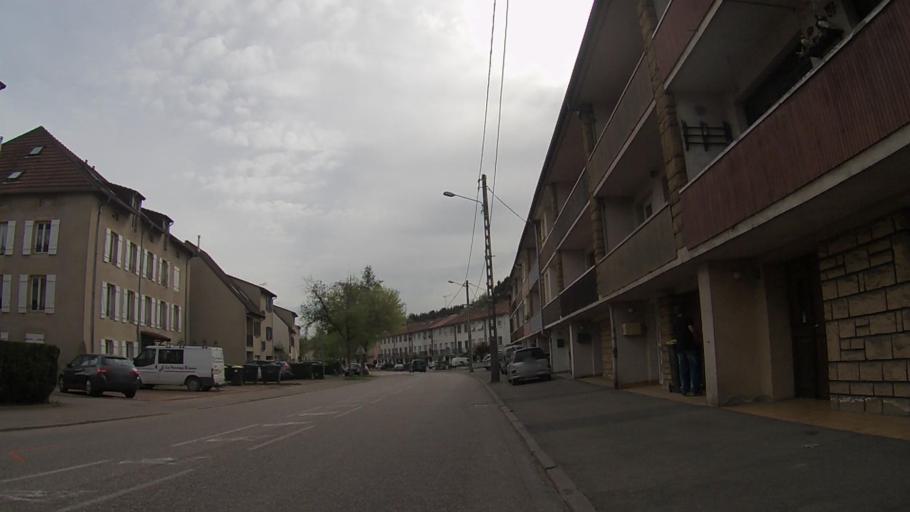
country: FR
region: Lorraine
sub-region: Departement de la Moselle
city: Ars-sur-Moselle
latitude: 49.0750
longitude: 6.0750
